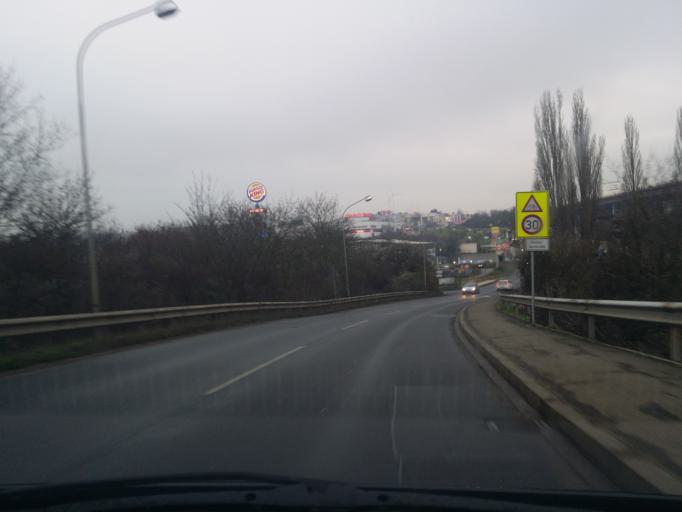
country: DE
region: Rheinland-Pfalz
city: Alzey
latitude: 49.7505
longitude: 8.1331
